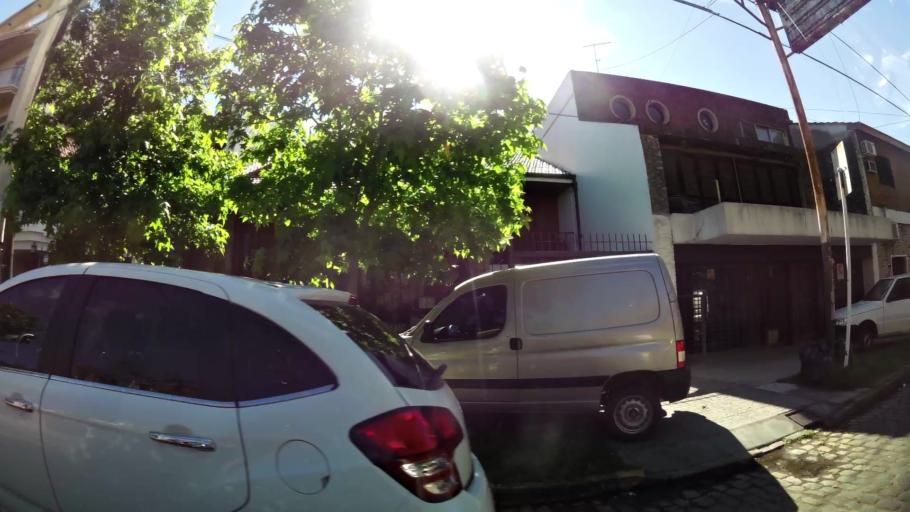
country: AR
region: Buenos Aires
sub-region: Partido de Lomas de Zamora
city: Lomas de Zamora
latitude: -34.7553
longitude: -58.4061
